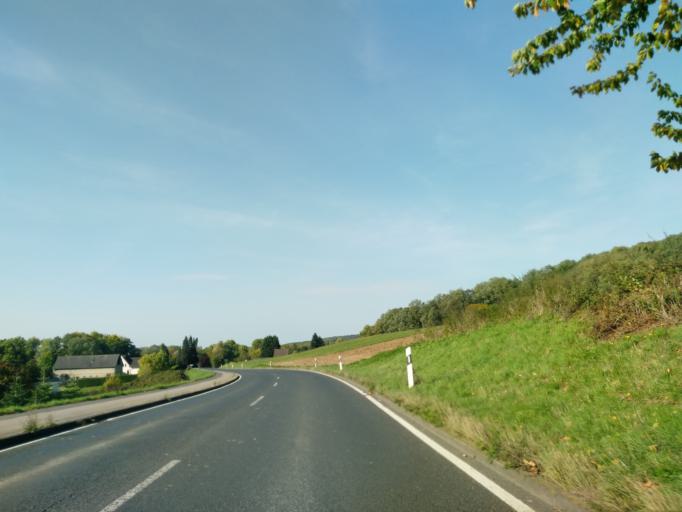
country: DE
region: North Rhine-Westphalia
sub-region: Regierungsbezirk Koln
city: Stossdorf
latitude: 50.7352
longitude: 7.2559
